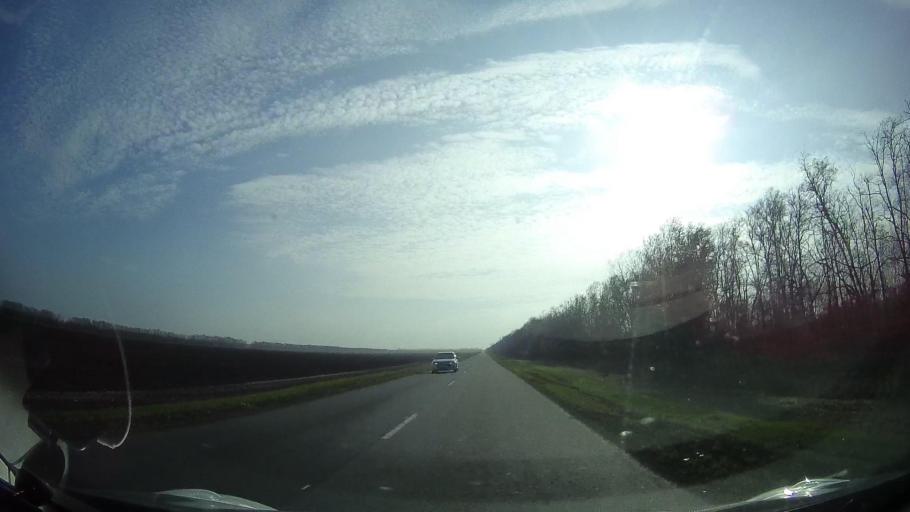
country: RU
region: Rostov
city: Mechetinskaya
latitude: 46.8865
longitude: 40.5419
